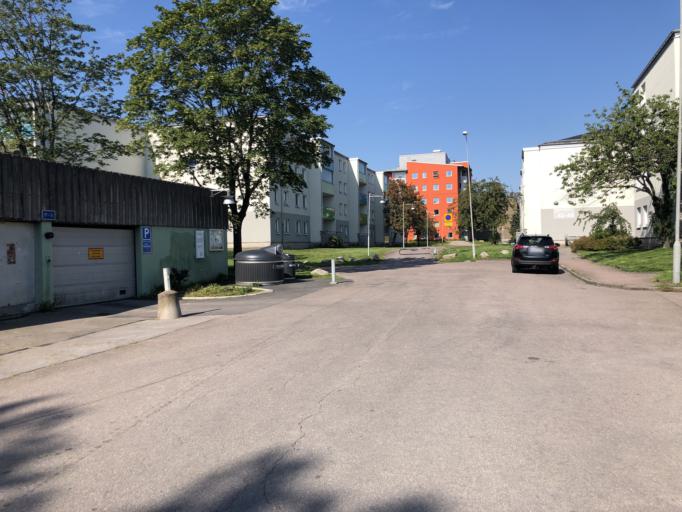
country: SE
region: Vaestra Goetaland
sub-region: Goteborg
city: Goeteborg
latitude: 57.7422
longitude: 11.9737
